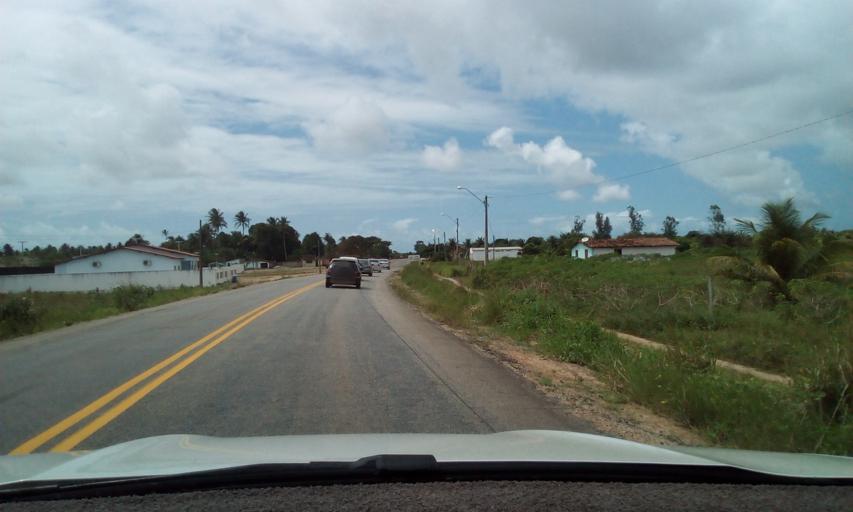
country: BR
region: Paraiba
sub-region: Rio Tinto
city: Rio Tinto
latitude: -6.7696
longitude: -35.0217
